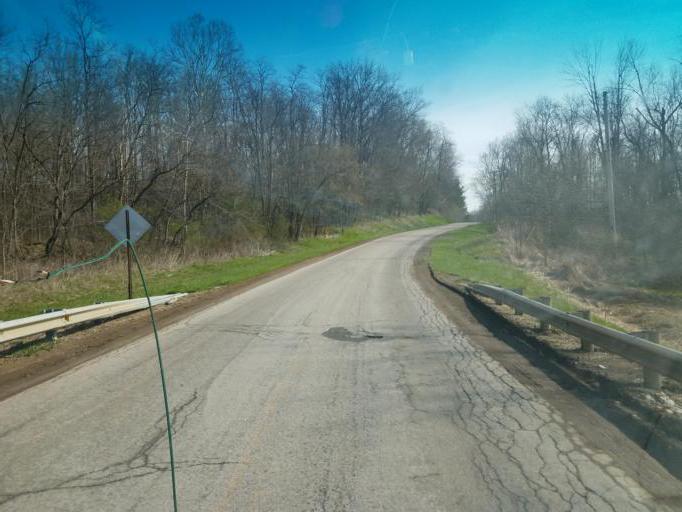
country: US
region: Ohio
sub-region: Richland County
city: Lincoln Heights
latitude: 40.8750
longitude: -82.4799
